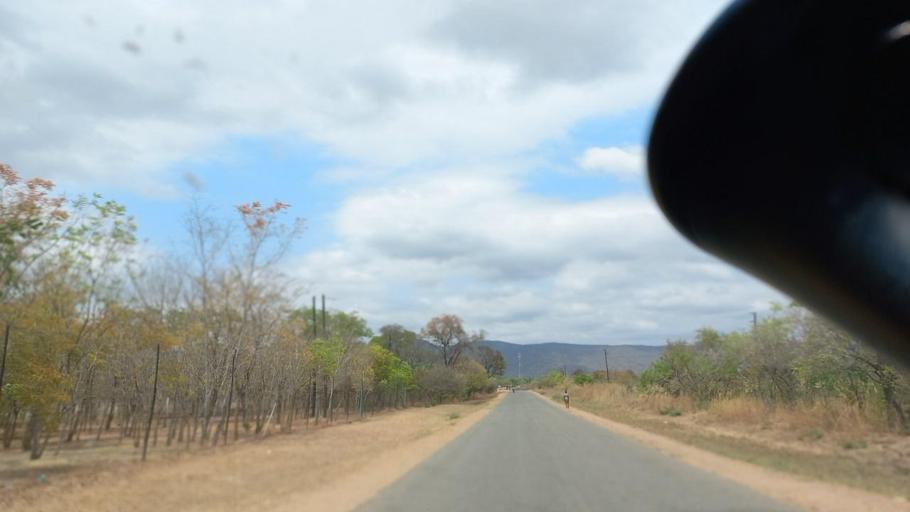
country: ZM
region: Lusaka
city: Luangwa
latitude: -15.1017
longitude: 29.7299
